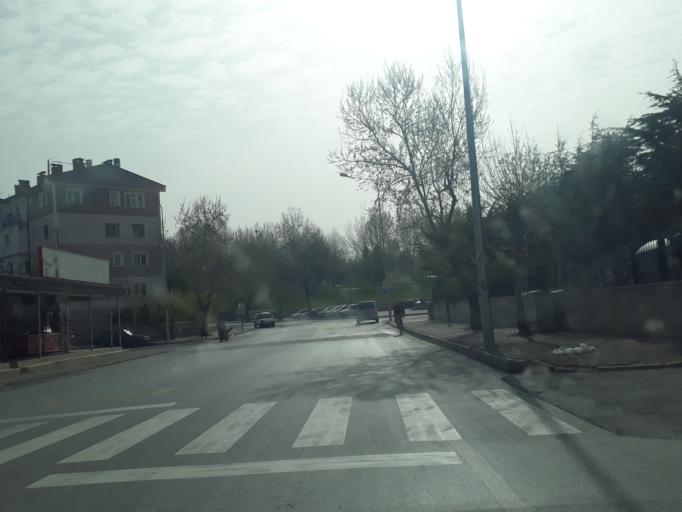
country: TR
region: Konya
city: Selcuklu
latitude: 37.9325
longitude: 32.4979
